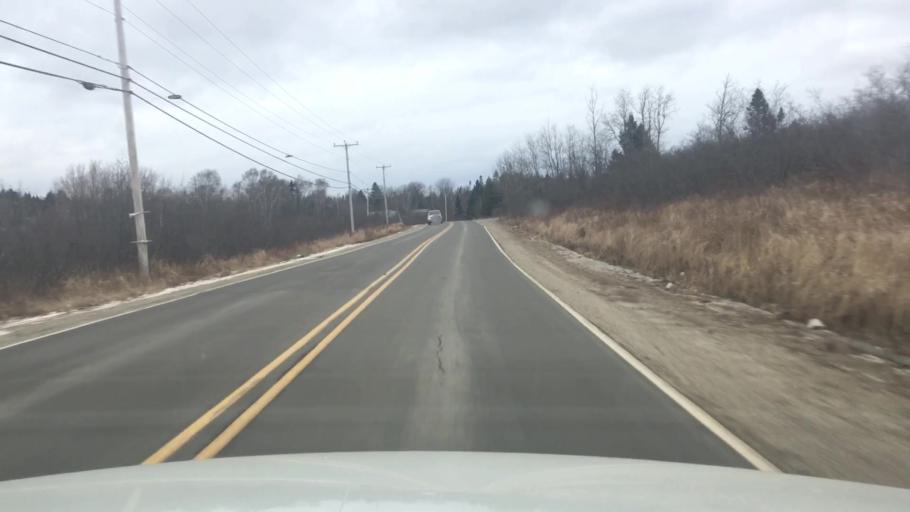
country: US
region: Maine
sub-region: Washington County
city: Jonesport
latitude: 44.5551
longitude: -67.6259
